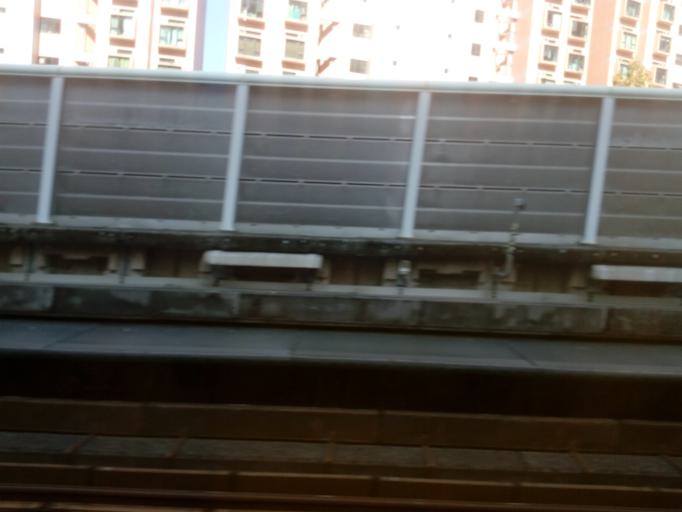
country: HK
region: Sai Kung
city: Sai Kung
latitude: 22.4259
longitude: 114.2370
